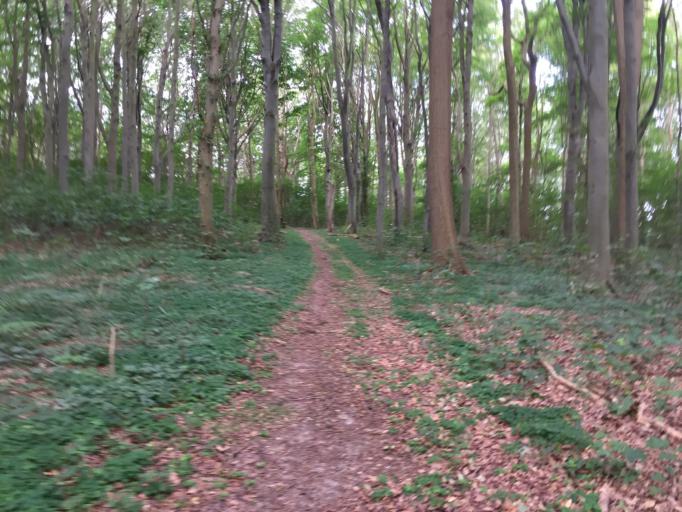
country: DK
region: South Denmark
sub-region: Assens Kommune
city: Harby
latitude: 55.1424
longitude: 10.0314
